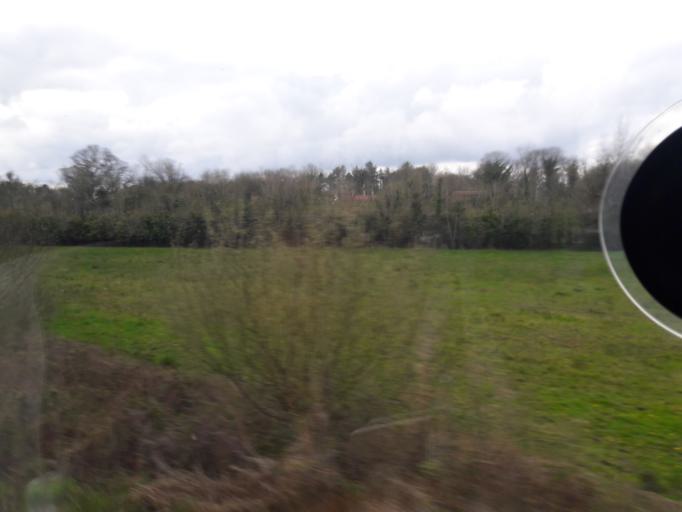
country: IE
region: Leinster
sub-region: An Longfort
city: Longford
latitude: 53.7375
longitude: -7.8210
